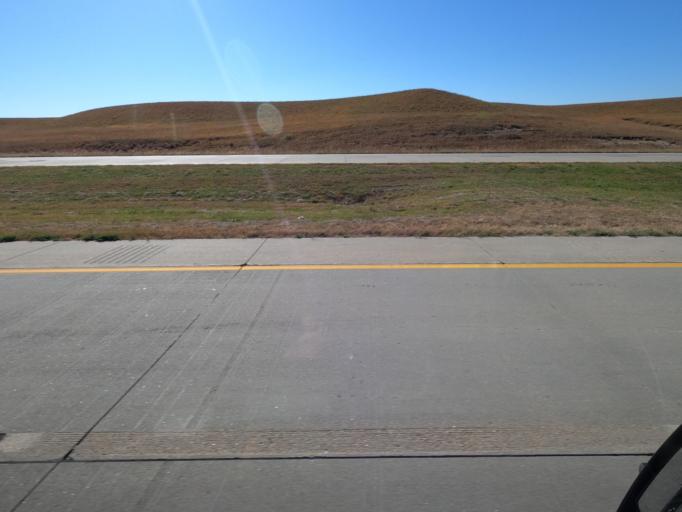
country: US
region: Kansas
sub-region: Riley County
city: Manhattan
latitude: 39.0667
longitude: -96.5930
